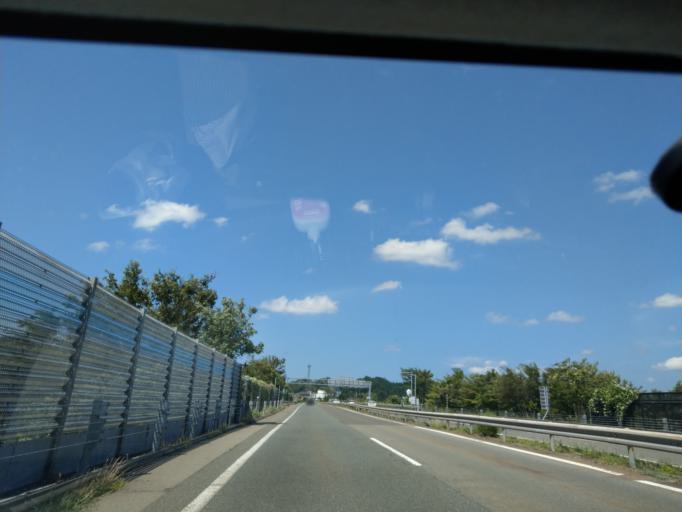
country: JP
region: Akita
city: Akita
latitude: 39.6476
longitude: 140.2076
